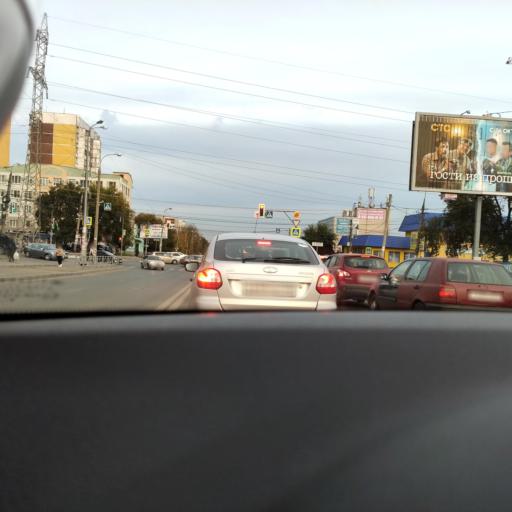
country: RU
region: Samara
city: Samara
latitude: 53.2064
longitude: 50.2125
